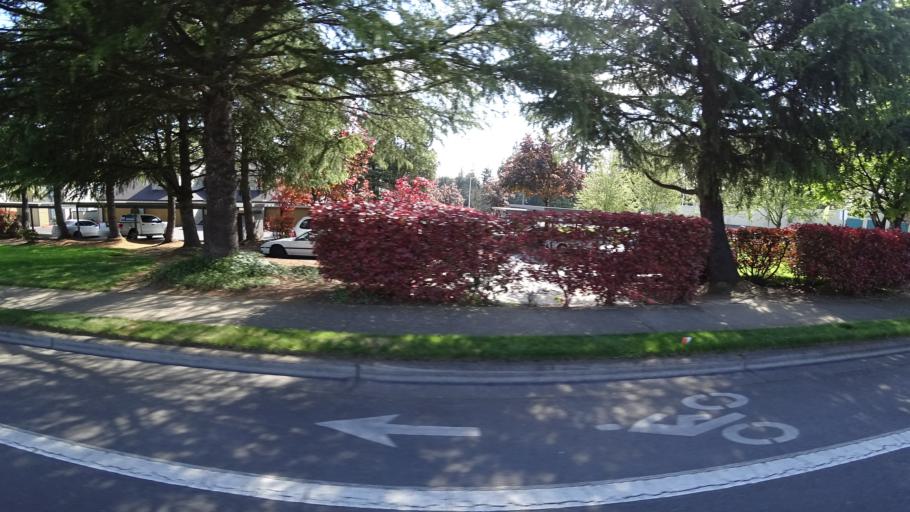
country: US
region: Oregon
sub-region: Washington County
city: King City
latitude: 45.4388
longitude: -122.8259
